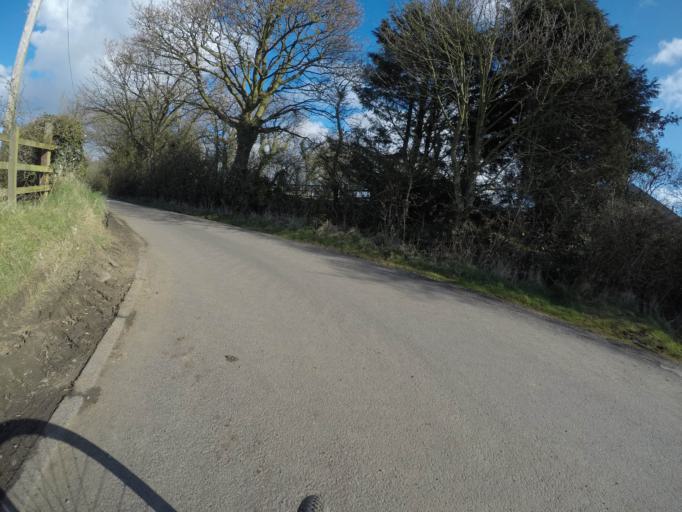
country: GB
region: Scotland
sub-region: North Ayrshire
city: Irvine
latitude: 55.6621
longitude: -4.6488
